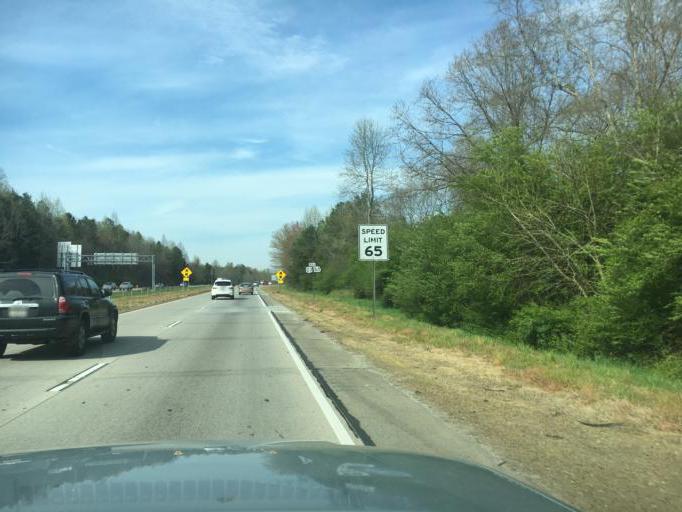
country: US
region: Georgia
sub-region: Hall County
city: Gainesville
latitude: 34.3242
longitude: -83.7869
